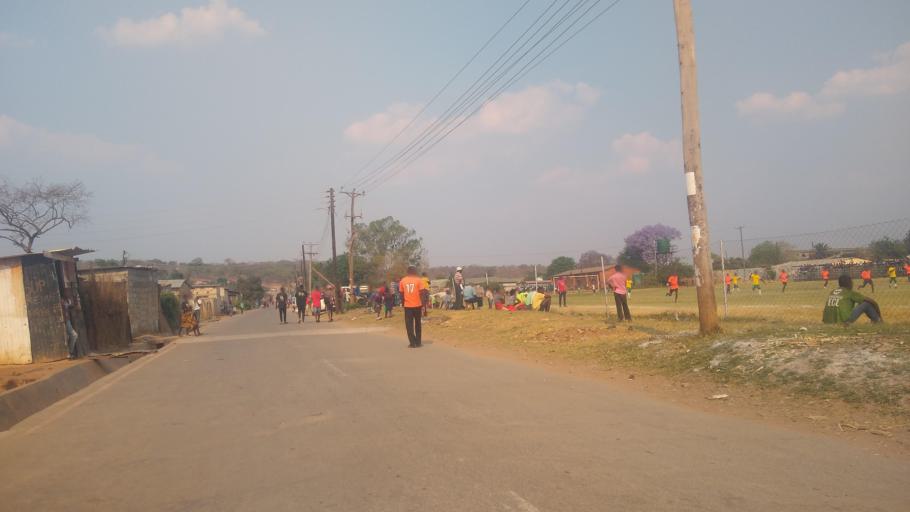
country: ZM
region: Lusaka
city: Lusaka
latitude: -15.4466
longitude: 28.3837
